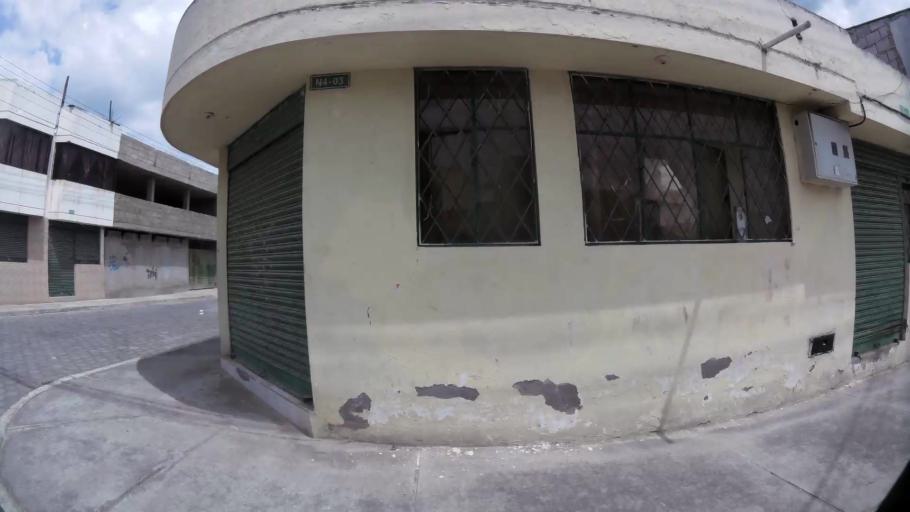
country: EC
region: Pichincha
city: Quito
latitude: -0.0819
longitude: -78.4133
